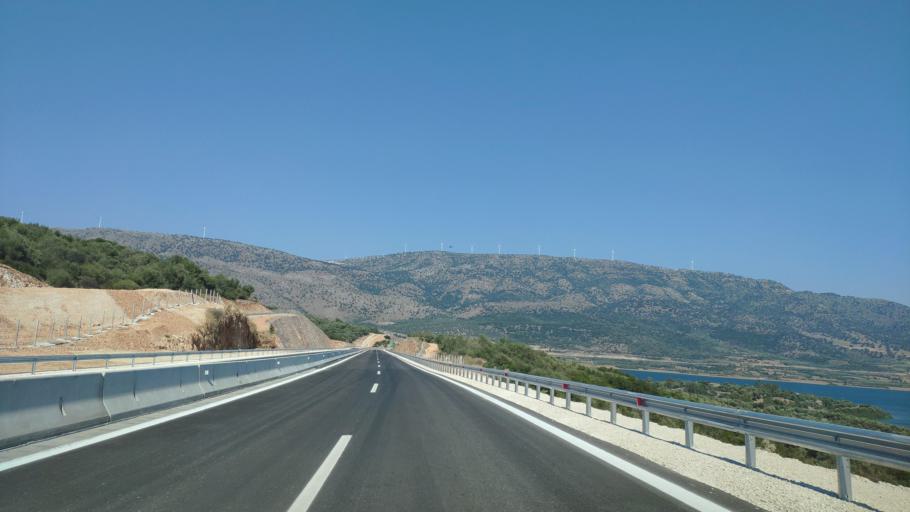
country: GR
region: West Greece
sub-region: Nomos Aitolias kai Akarnanias
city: Stanos
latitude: 38.7713
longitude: 21.1622
